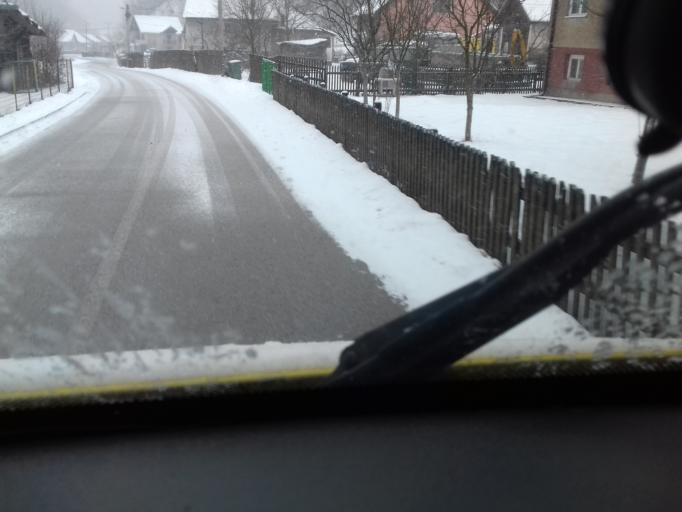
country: BA
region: Federation of Bosnia and Herzegovina
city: Zeljezno Polje
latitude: 44.3332
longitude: 17.9013
